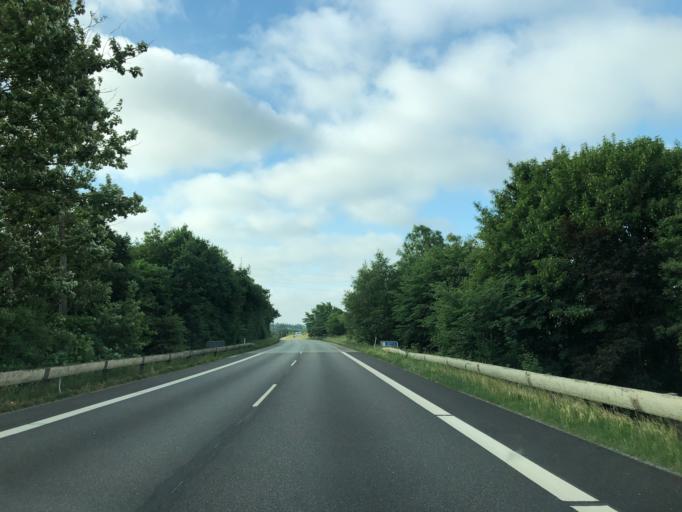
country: DK
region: South Denmark
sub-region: Kolding Kommune
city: Kolding
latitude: 55.5750
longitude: 9.4331
